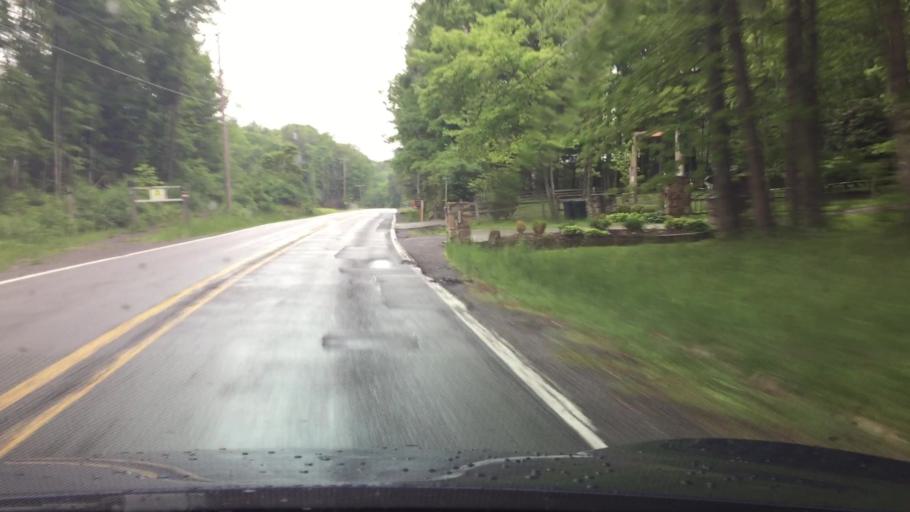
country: US
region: West Virginia
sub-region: Raleigh County
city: Shady Spring
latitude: 37.6902
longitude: -81.0619
